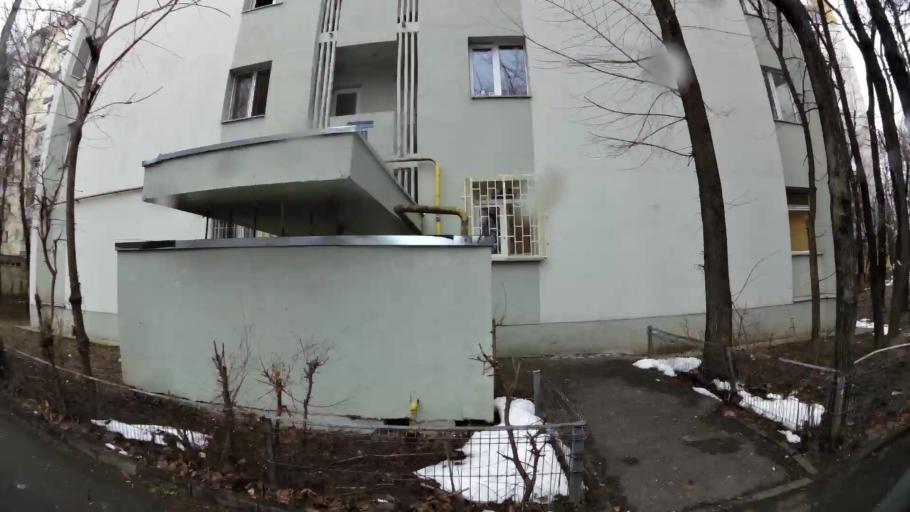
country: RO
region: Ilfov
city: Dobroesti
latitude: 44.4355
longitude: 26.1656
